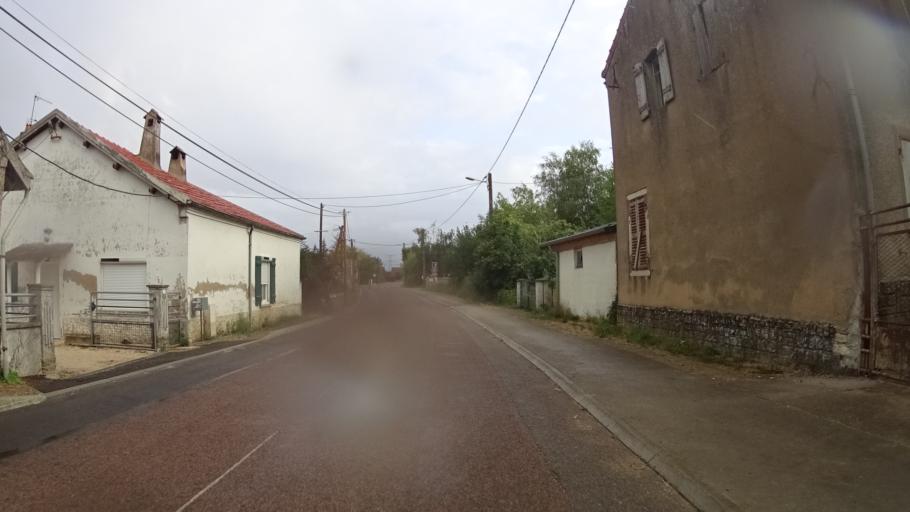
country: FR
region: Bourgogne
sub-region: Departement de Saone-et-Loire
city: Verdun-sur-le-Doubs
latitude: 46.9599
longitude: 5.0270
